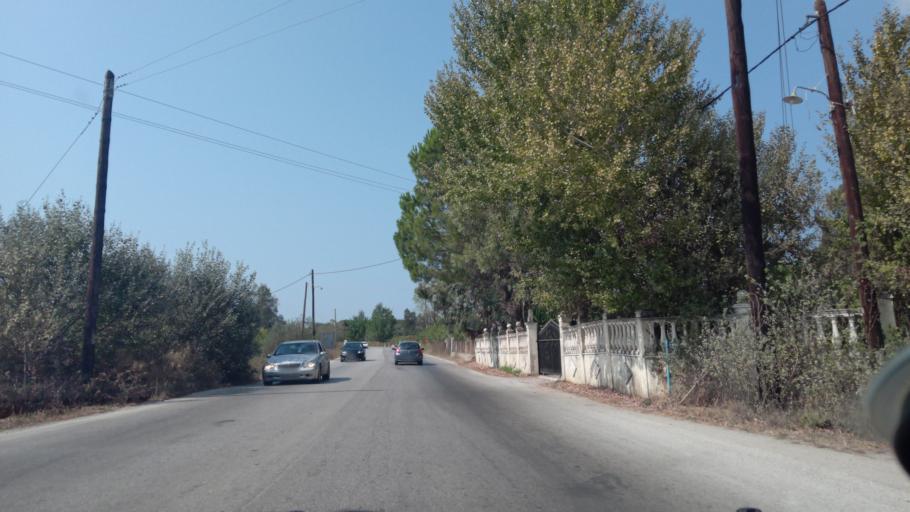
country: GR
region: Ionian Islands
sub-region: Nomos Kerkyras
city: Perivoli
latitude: 39.4215
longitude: 20.0375
